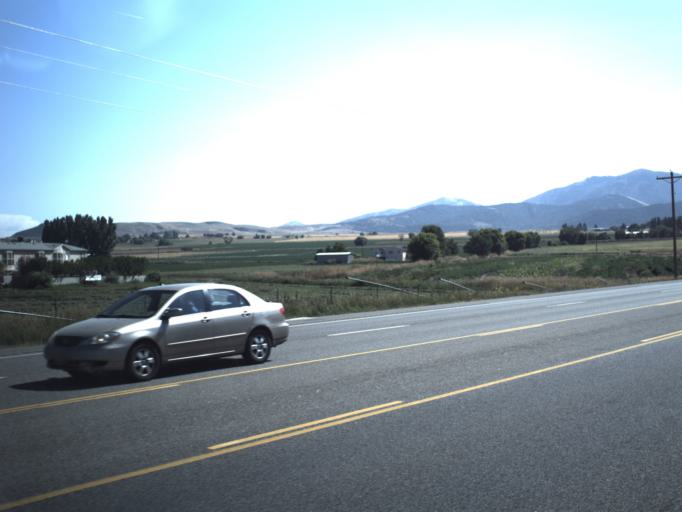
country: US
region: Utah
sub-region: Cache County
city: Wellsville
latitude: 41.6268
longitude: -111.9257
